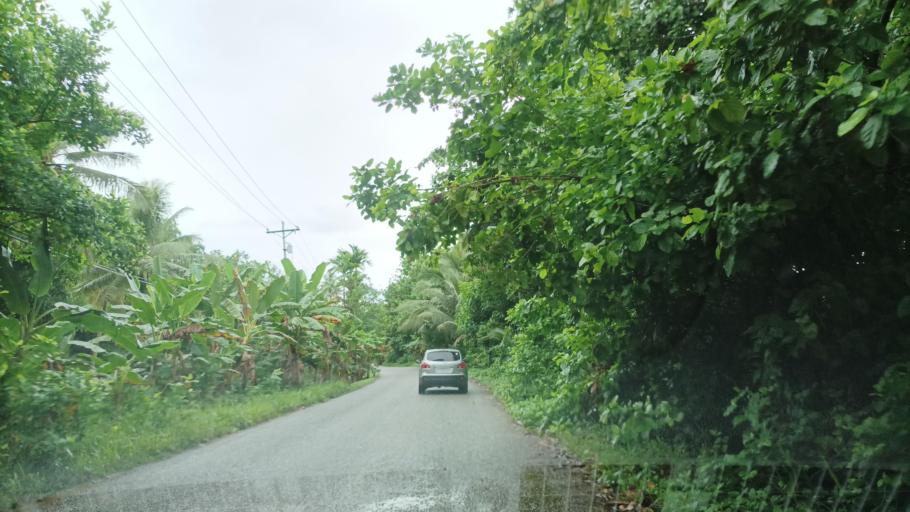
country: FM
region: Kosrae
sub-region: Lelu Municipality
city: Lelu
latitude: 5.3430
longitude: 163.0196
